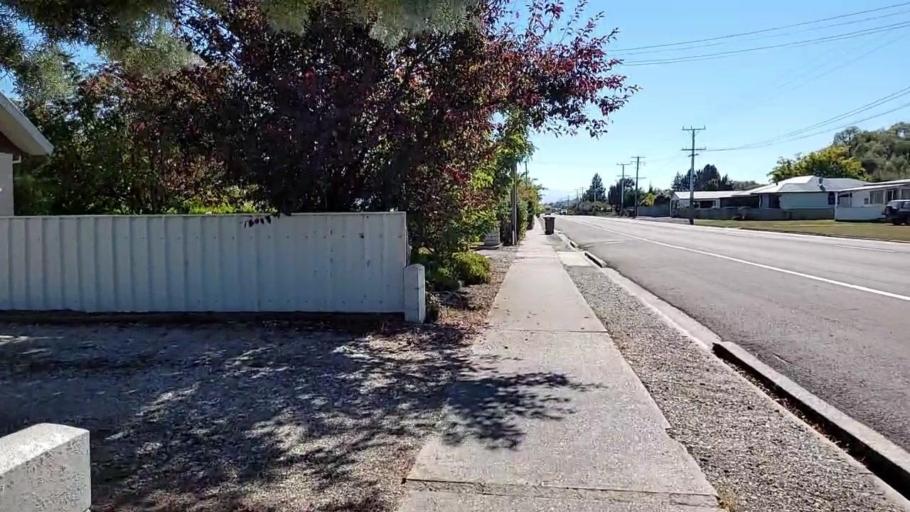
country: NZ
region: Otago
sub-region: Queenstown-Lakes District
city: Wanaka
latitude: -45.1036
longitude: 169.5952
